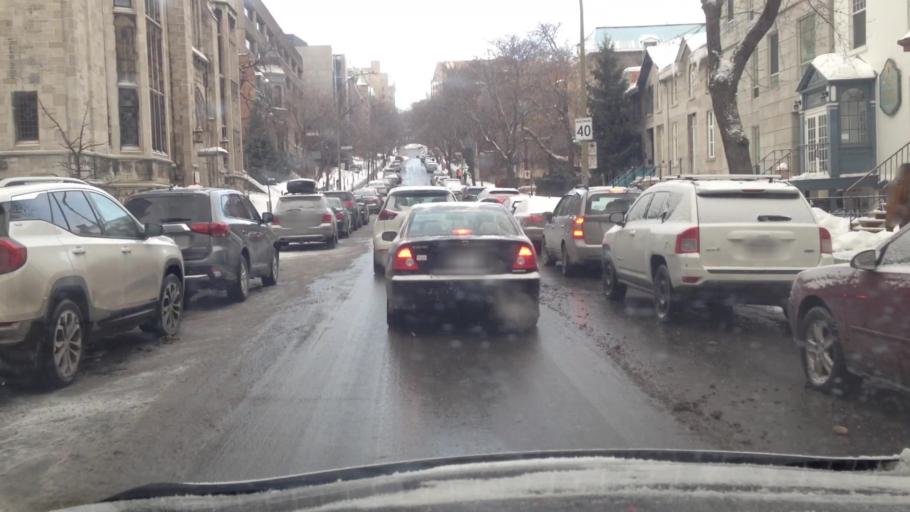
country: CA
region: Quebec
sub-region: Montreal
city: Montreal
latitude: 45.5066
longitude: -73.5767
